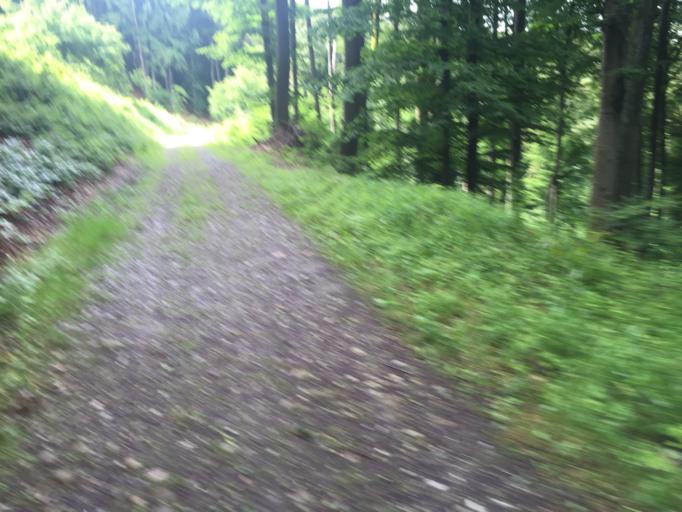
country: CH
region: Bern
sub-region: Bern-Mittelland District
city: Koniz
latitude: 46.9349
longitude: 7.3981
